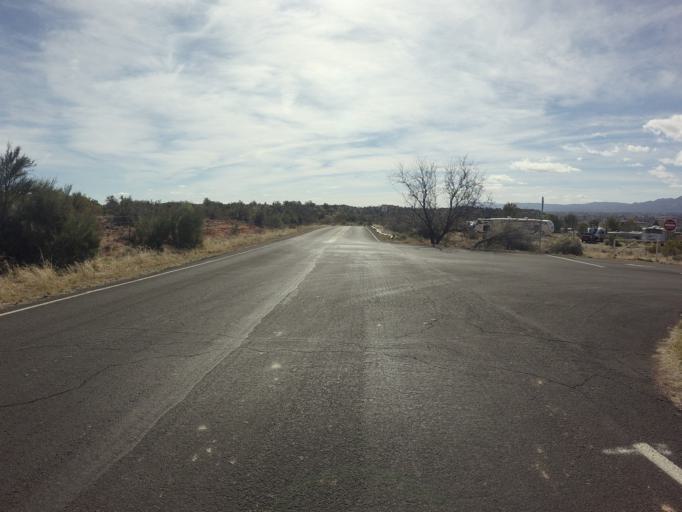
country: US
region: Arizona
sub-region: Yavapai County
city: Cottonwood
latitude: 34.7620
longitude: -112.0153
